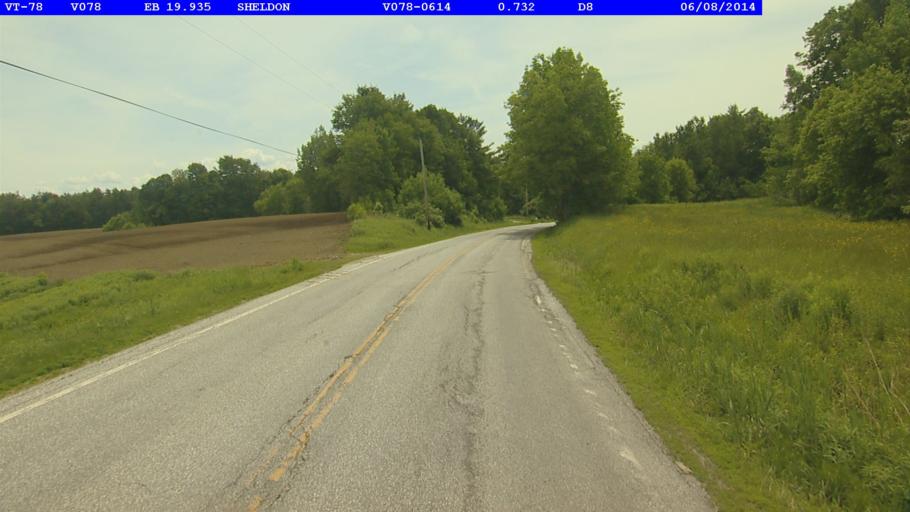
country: US
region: Vermont
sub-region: Franklin County
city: Enosburg Falls
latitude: 44.9160
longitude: -72.9594
